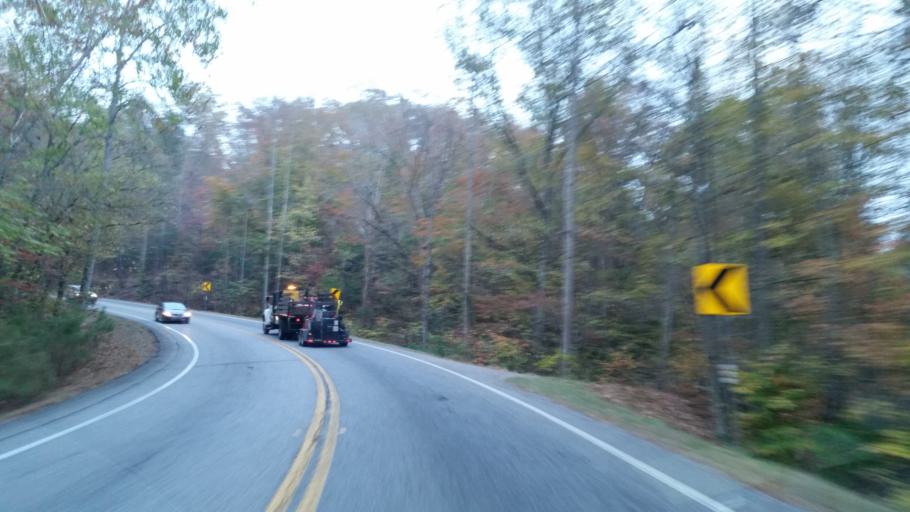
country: US
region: Georgia
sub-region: Gilmer County
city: Ellijay
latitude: 34.5778
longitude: -84.6473
